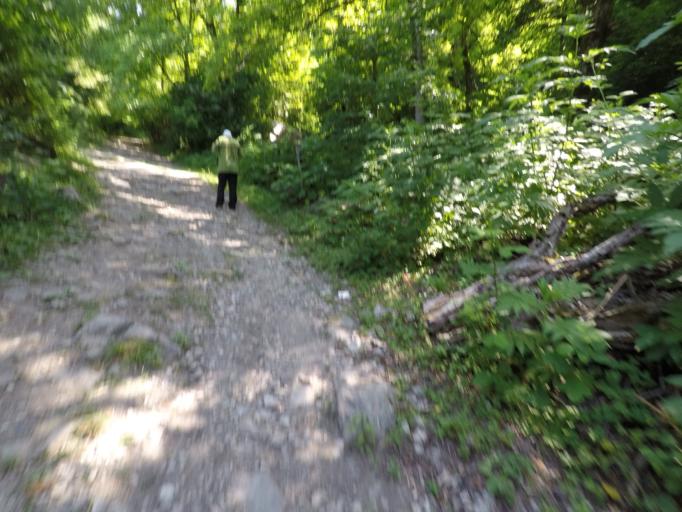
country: AZ
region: Qakh Rayon
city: Cinarli
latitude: 41.4903
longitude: 46.8579
